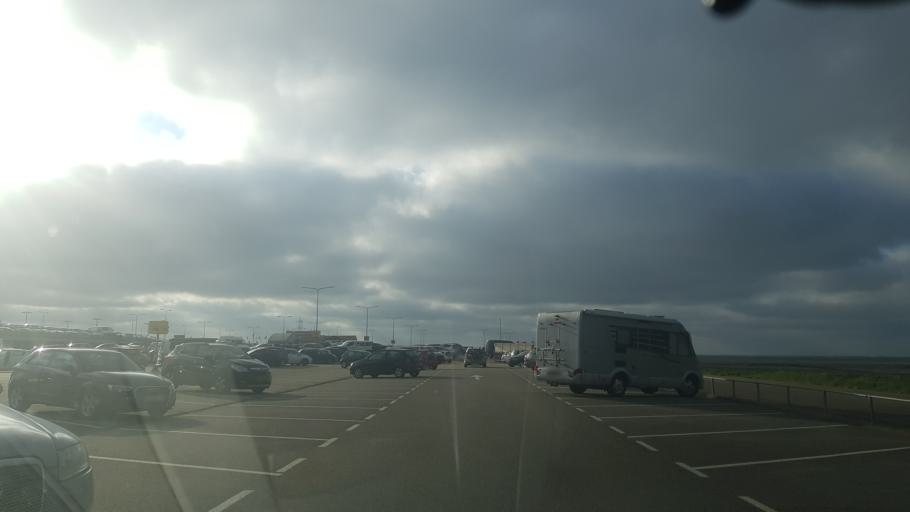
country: NL
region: Friesland
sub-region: Gemeente Dongeradeel
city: Holwerd
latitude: 53.3926
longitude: 5.8837
